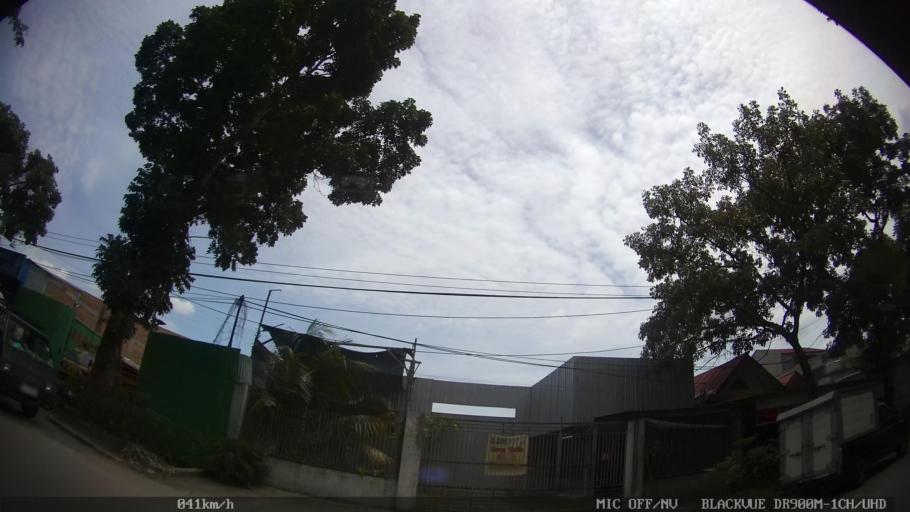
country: ID
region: North Sumatra
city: Sunggal
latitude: 3.5407
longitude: 98.6452
